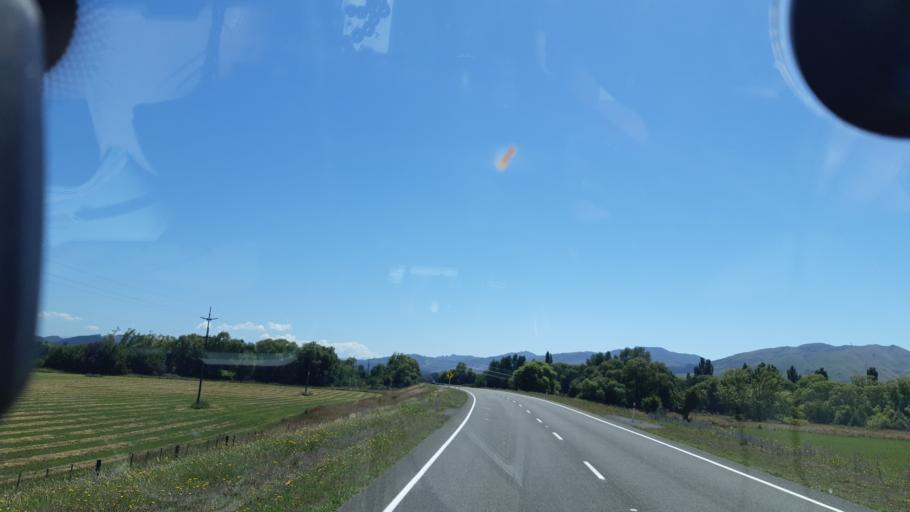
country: NZ
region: Canterbury
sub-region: Kaikoura District
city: Kaikoura
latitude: -42.7273
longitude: 173.2786
